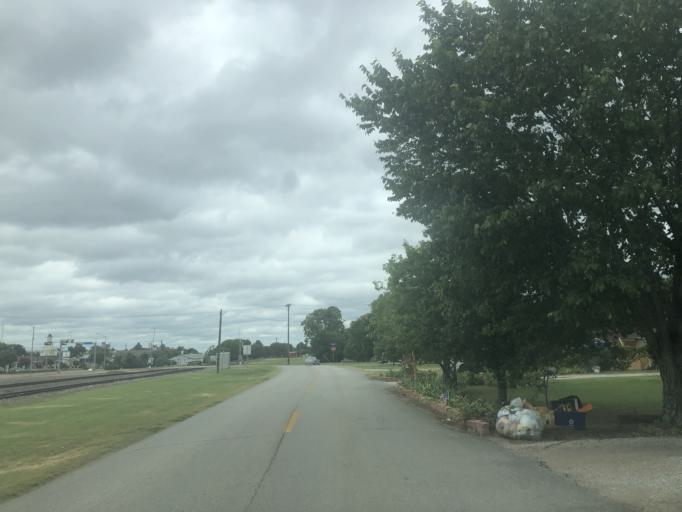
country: US
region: Texas
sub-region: Dallas County
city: Duncanville
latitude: 32.6558
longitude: -96.9085
